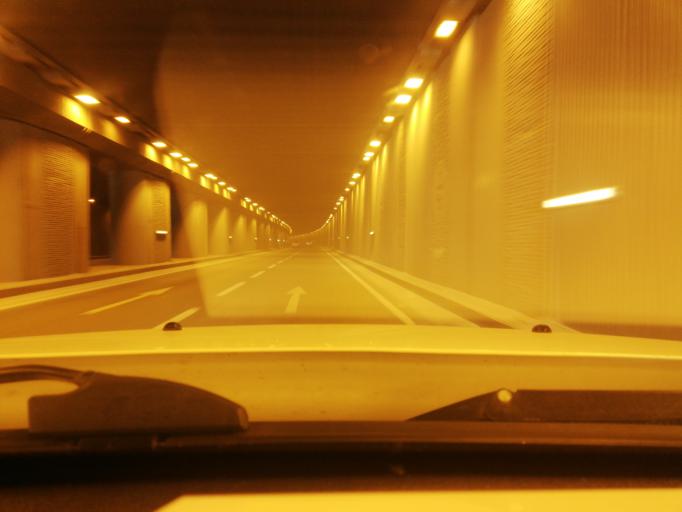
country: TR
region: Kocaeli
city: Izmit
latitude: 40.7643
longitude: 29.9139
